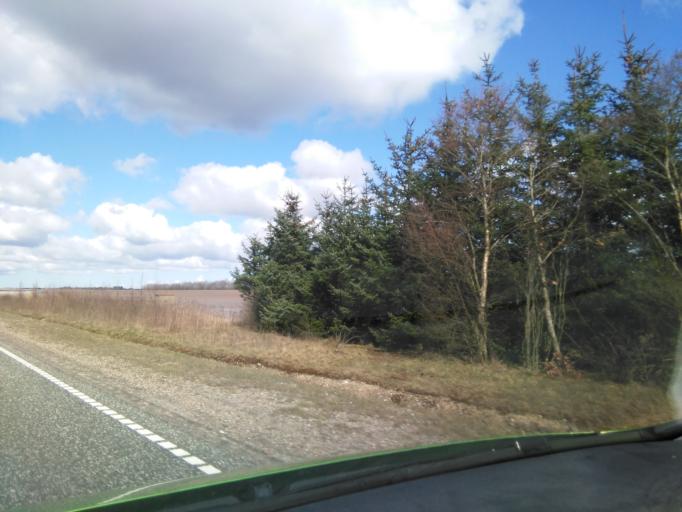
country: DK
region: Central Jutland
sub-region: Ikast-Brande Kommune
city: Bording Kirkeby
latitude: 56.1238
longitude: 9.3535
